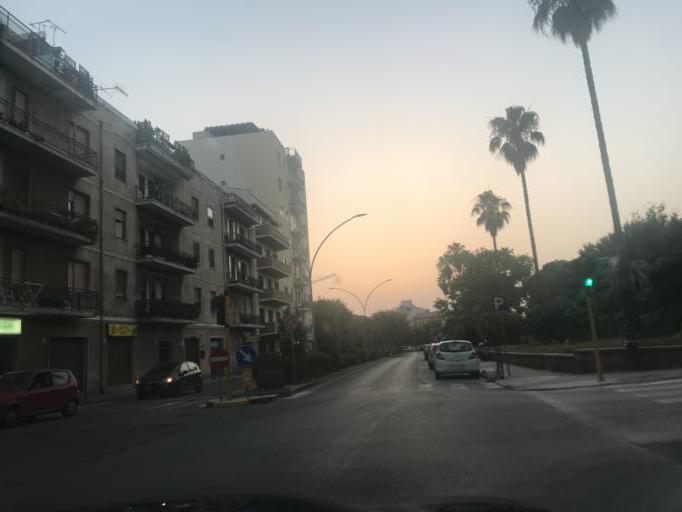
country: IT
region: Sardinia
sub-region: Provincia di Sassari
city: Alghero
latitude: 40.5550
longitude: 8.3203
